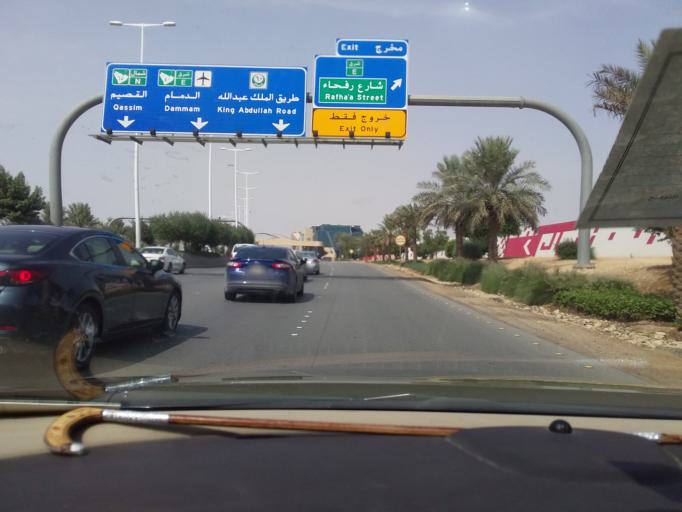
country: SA
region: Ar Riyad
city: Riyadh
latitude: 24.7313
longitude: 46.7091
